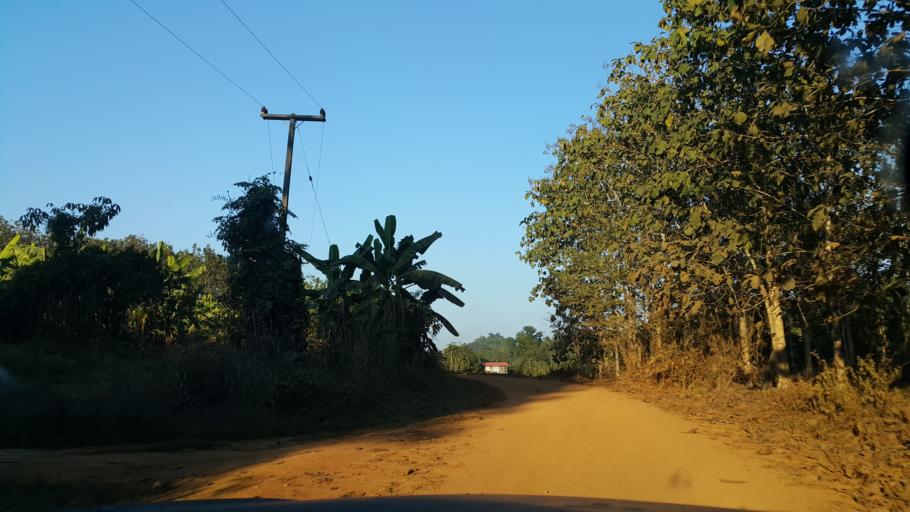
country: TH
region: Sukhothai
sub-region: Amphoe Si Satchanalai
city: Si Satchanalai
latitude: 17.6115
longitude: 99.6206
